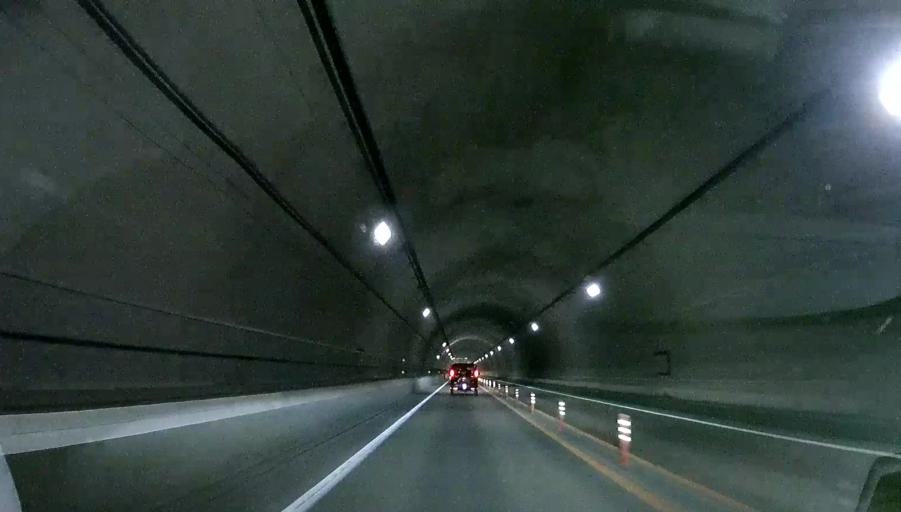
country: JP
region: Hokkaido
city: Shimo-furano
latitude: 43.0499
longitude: 142.4915
